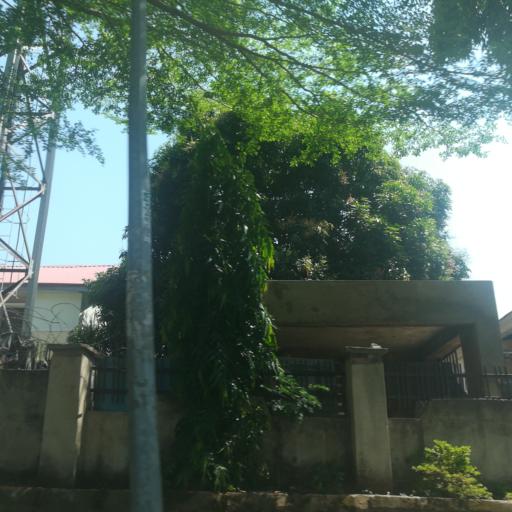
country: NG
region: Abuja Federal Capital Territory
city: Abuja
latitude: 9.0737
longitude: 7.4512
